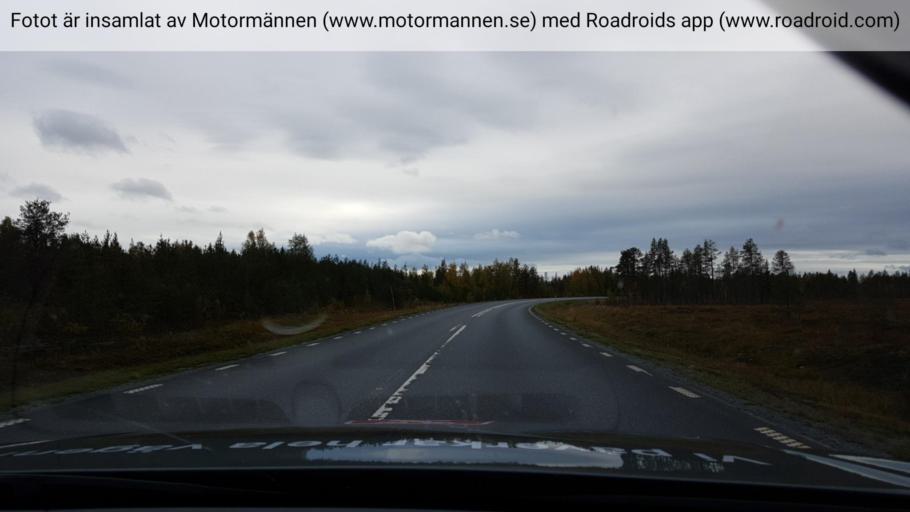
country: SE
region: Vaesterbotten
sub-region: Dorotea Kommun
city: Dorotea
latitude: 64.3375
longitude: 16.6413
